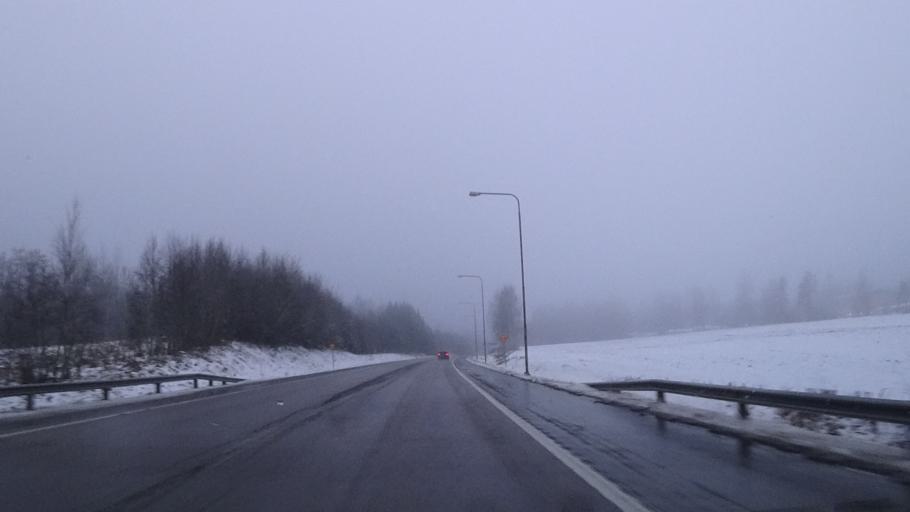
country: FI
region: Paijanne Tavastia
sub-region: Lahti
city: Hollola
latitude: 60.9832
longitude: 25.4351
